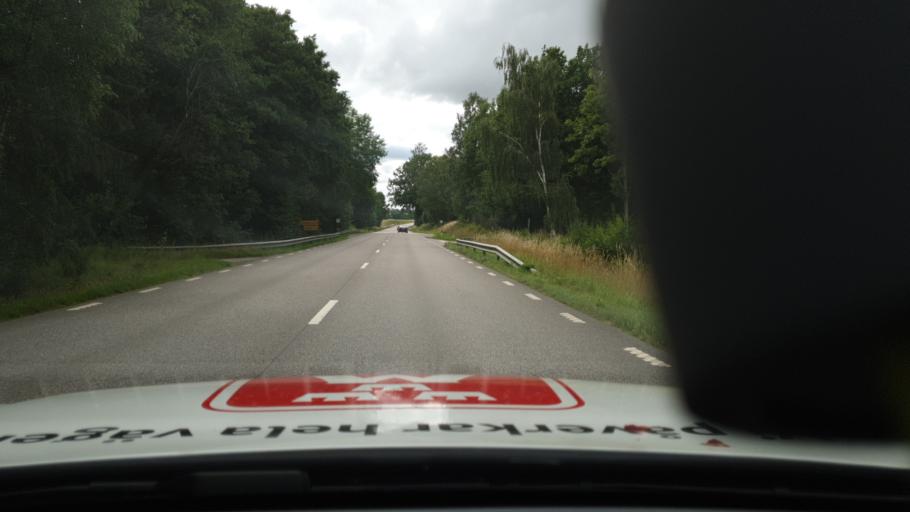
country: SE
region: Vaestra Goetaland
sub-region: Grastorps Kommun
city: Graestorp
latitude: 58.3283
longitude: 12.7056
